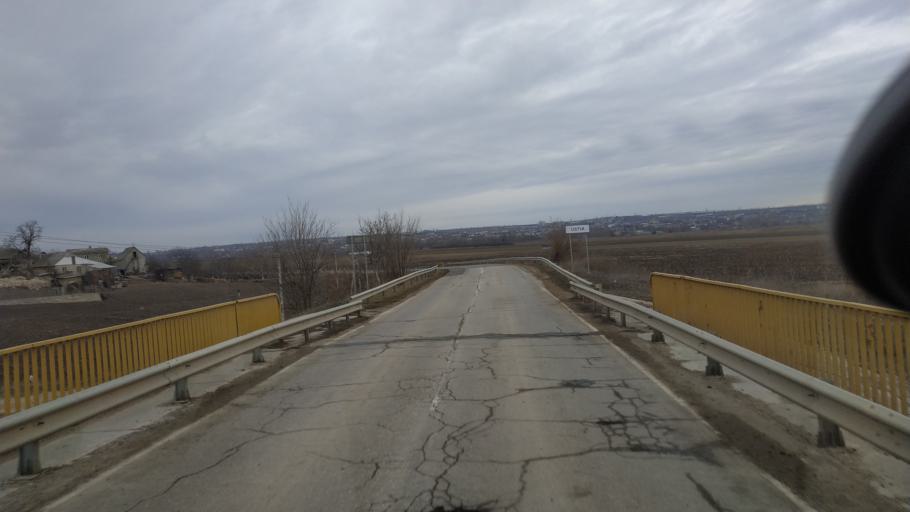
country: MD
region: Telenesti
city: Dubasari
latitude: 47.2526
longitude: 29.1357
